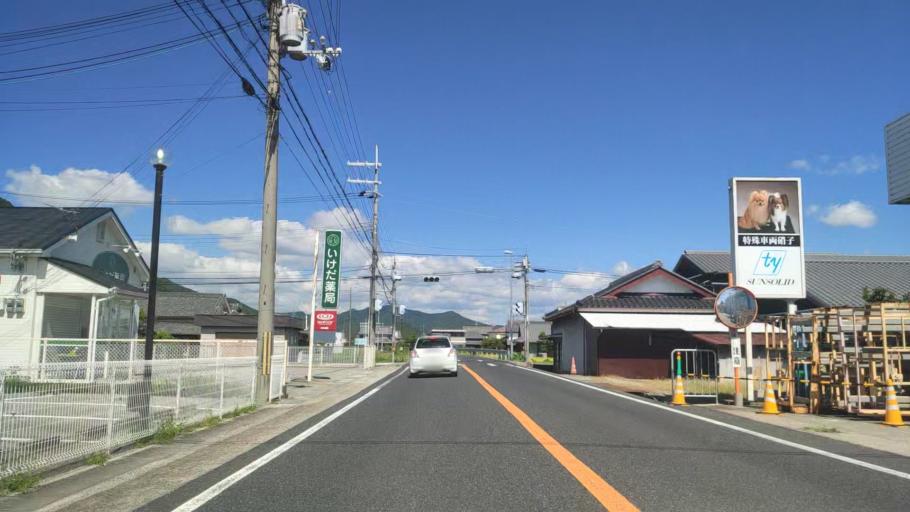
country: JP
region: Hyogo
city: Nishiwaki
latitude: 35.0098
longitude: 134.9915
